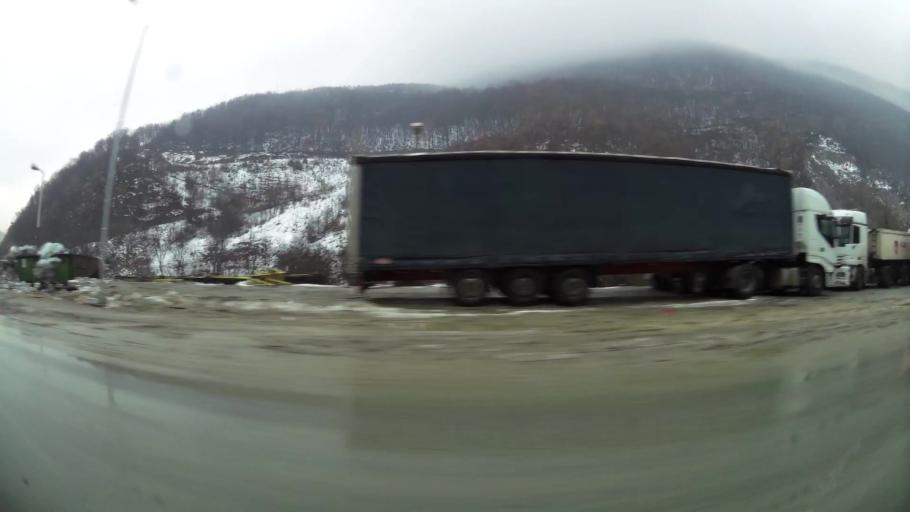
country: XK
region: Ferizaj
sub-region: Hani i Elezit
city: Hani i Elezit
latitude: 42.1581
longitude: 21.2892
